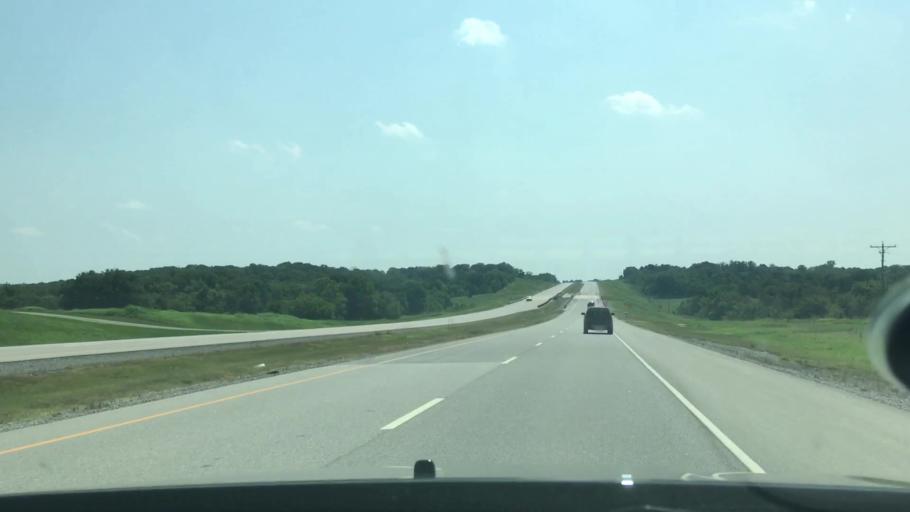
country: US
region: Oklahoma
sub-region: Atoka County
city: Atoka
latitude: 34.3557
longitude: -96.0901
